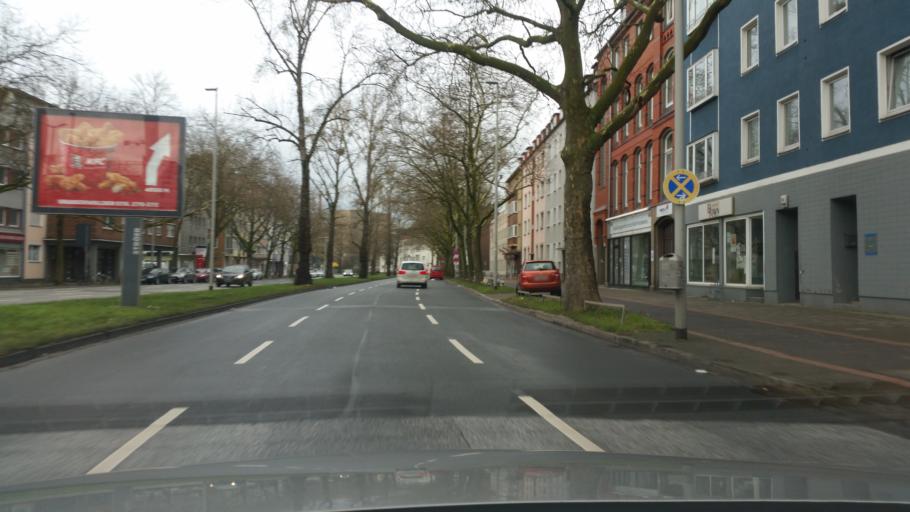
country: DE
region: Lower Saxony
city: Hannover
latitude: 52.3822
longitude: 9.7380
